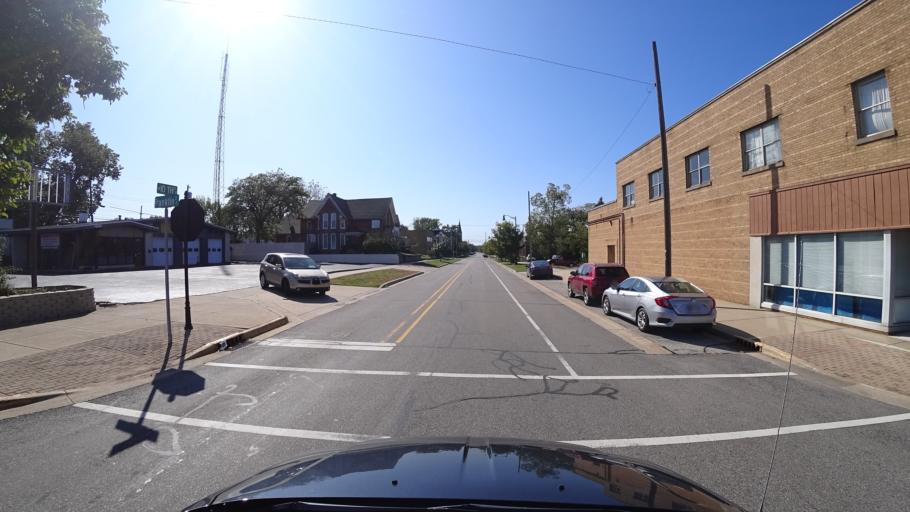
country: US
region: Indiana
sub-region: LaPorte County
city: Michigan City
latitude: 41.7121
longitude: -86.8994
